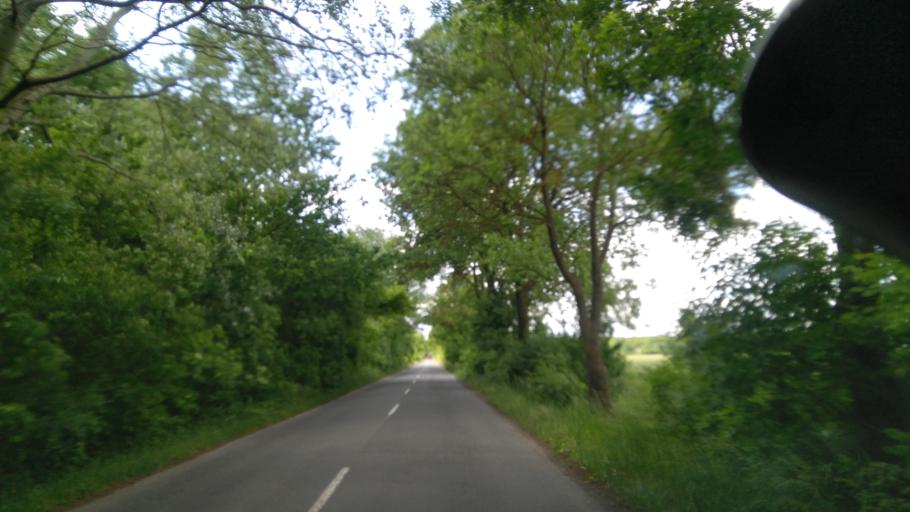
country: HU
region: Bekes
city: Bucsa
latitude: 47.1824
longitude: 21.0457
